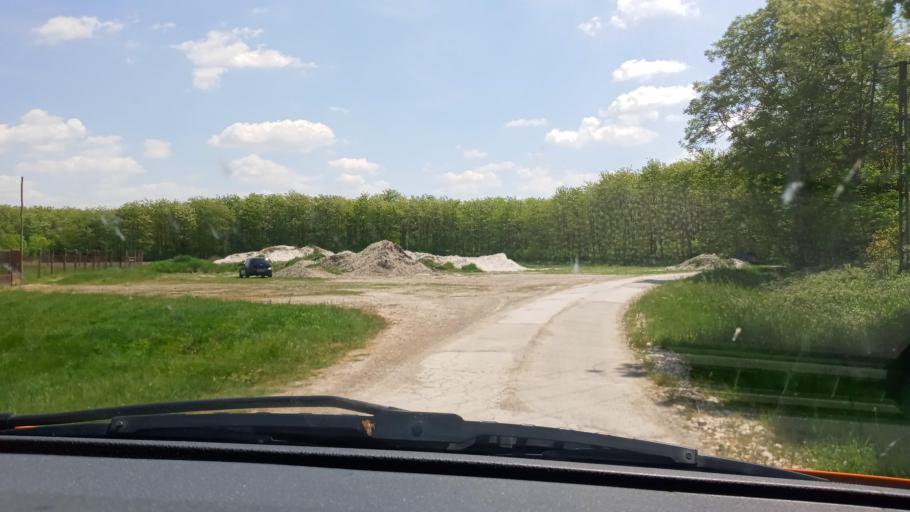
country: HU
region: Baranya
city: Siklos
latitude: 45.7703
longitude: 18.2868
